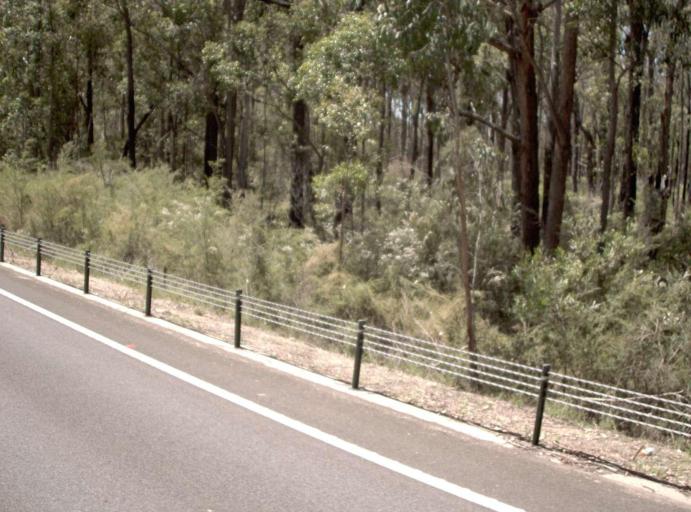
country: AU
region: Victoria
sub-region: East Gippsland
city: Lakes Entrance
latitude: -37.7474
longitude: 148.0716
